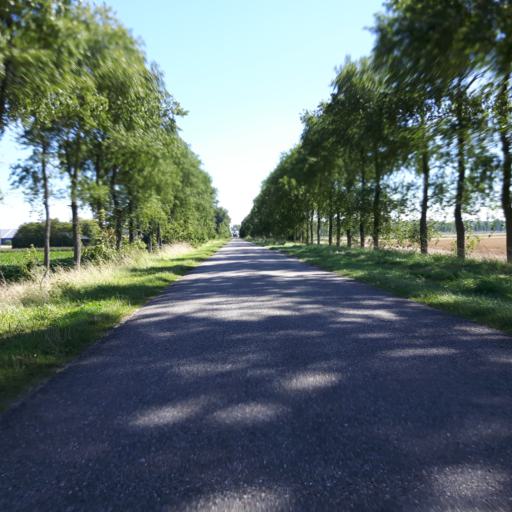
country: NL
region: Zeeland
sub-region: Gemeente Noord-Beveland
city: Kamperland
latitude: 51.5729
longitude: 3.7957
